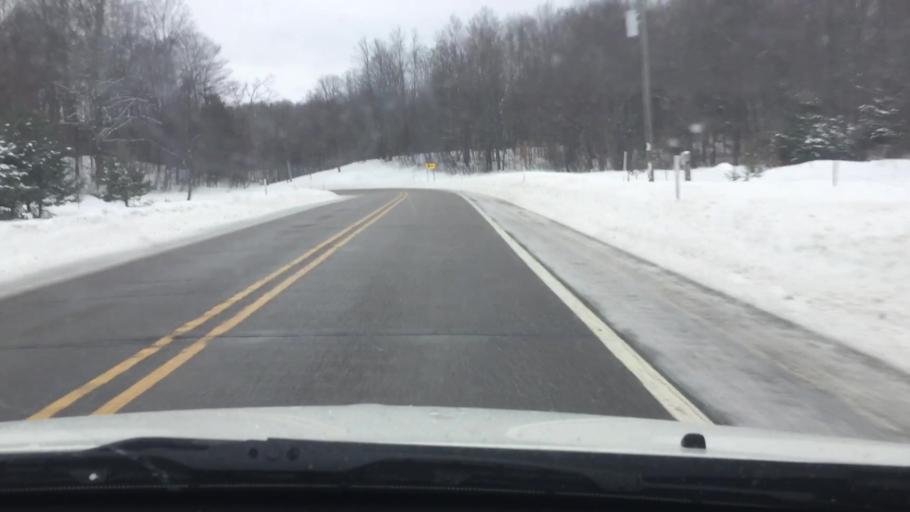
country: US
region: Michigan
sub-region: Charlevoix County
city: Boyne City
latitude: 45.0842
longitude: -84.9242
